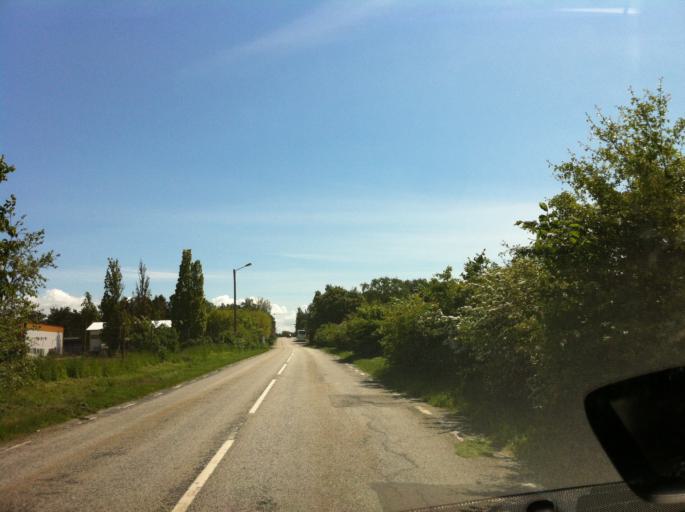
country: SE
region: Skane
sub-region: Kavlinge Kommun
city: Hofterup
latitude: 55.8265
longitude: 12.9671
